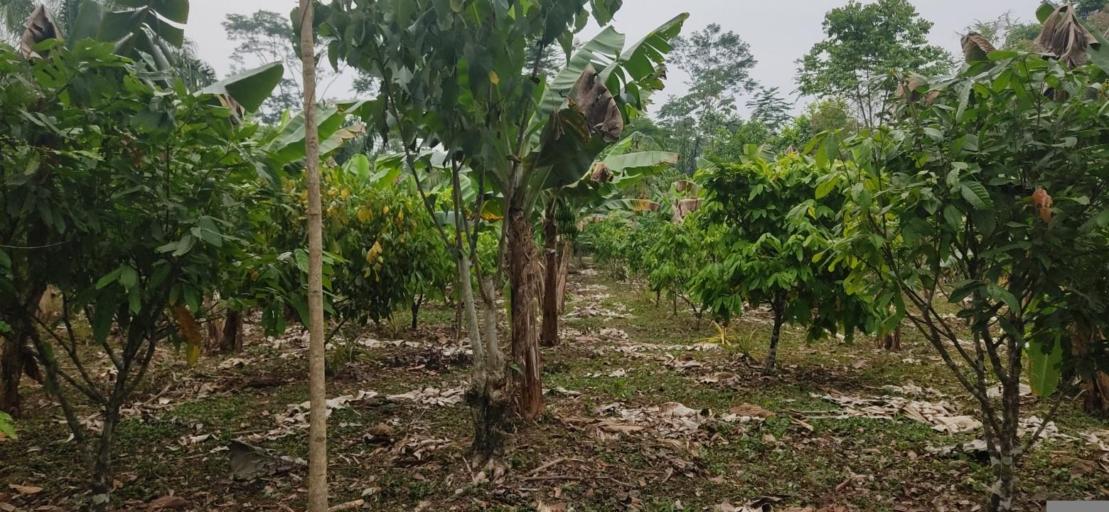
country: BO
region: La Paz
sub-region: Provincia Larecaja
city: Guanay
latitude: -15.5639
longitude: -67.3182
